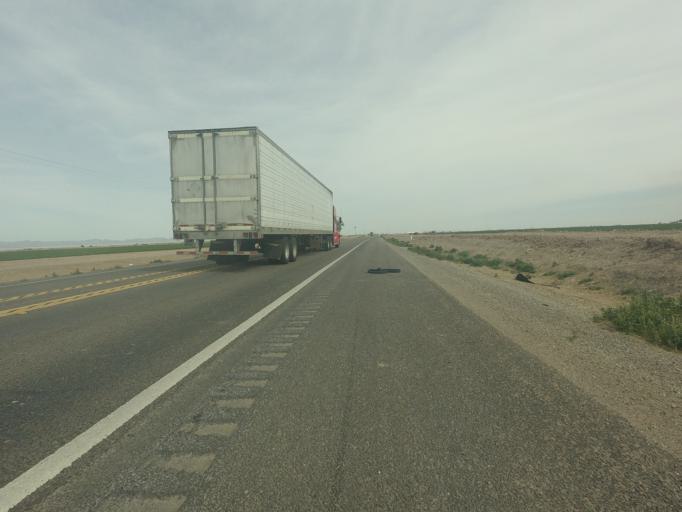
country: US
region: California
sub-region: Imperial County
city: Brawley
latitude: 32.9744
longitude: -115.4207
